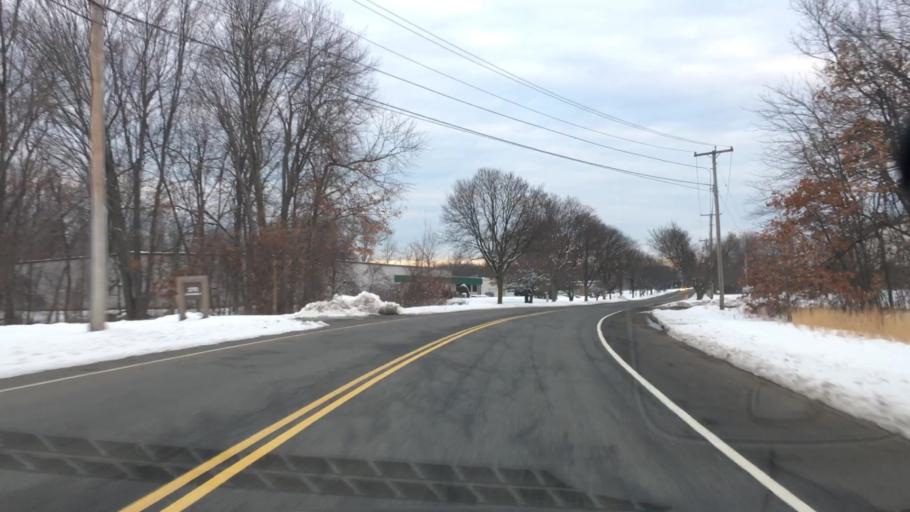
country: US
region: Massachusetts
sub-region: Hampden County
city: East Longmeadow
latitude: 42.0428
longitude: -72.5317
